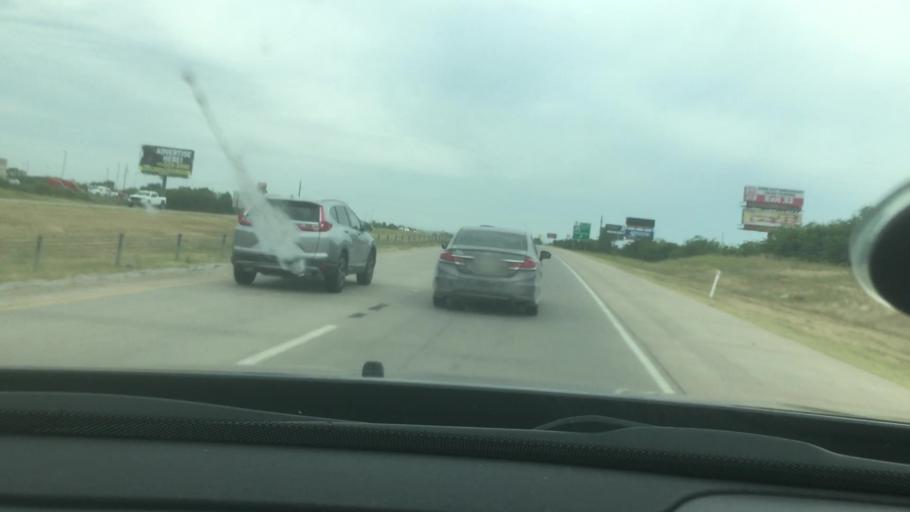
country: US
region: Oklahoma
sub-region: Carter County
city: Ardmore
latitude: 34.1950
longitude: -97.1640
